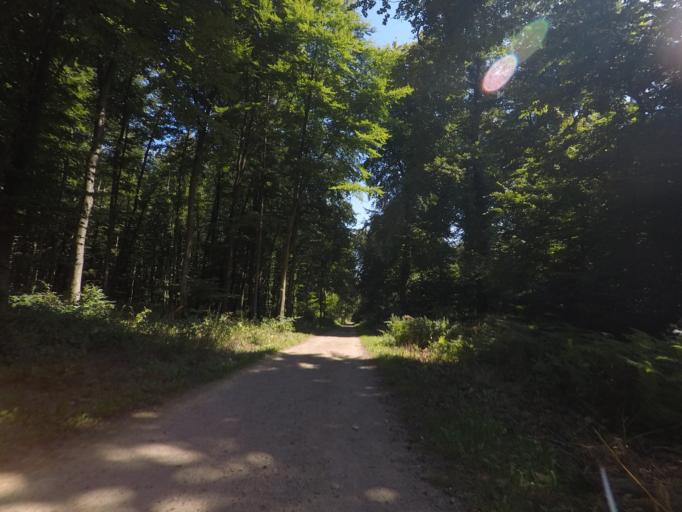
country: LU
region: Luxembourg
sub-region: Canton de Luxembourg
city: Strassen
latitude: 49.6316
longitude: 6.0791
